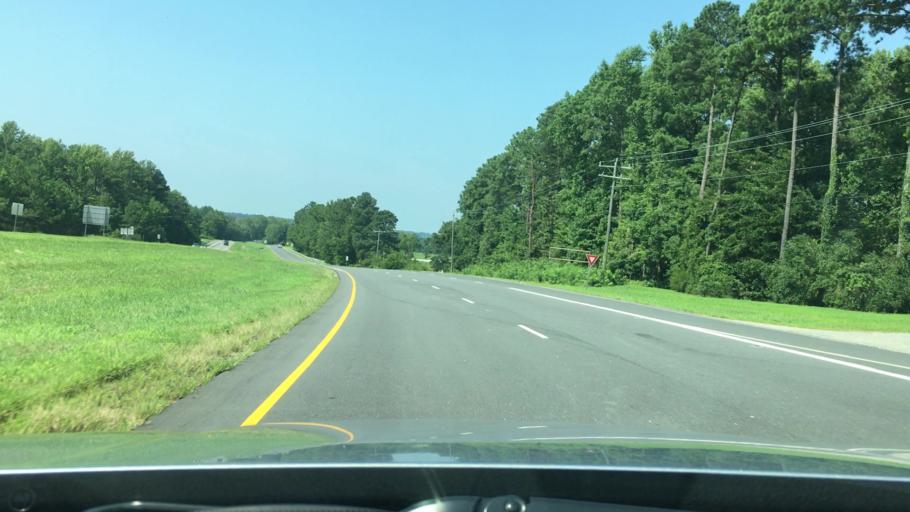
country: US
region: Virginia
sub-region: Caroline County
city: Bowling Green
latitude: 38.0395
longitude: -77.3634
